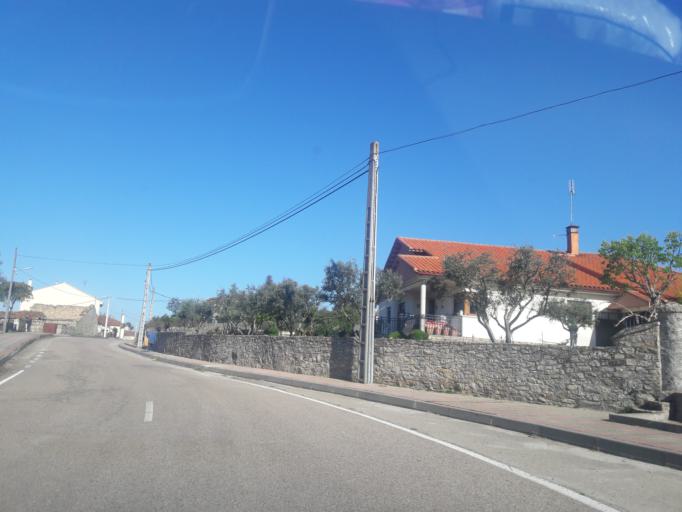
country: ES
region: Castille and Leon
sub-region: Provincia de Salamanca
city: Cabeza del Caballo
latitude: 41.1277
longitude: -6.5553
